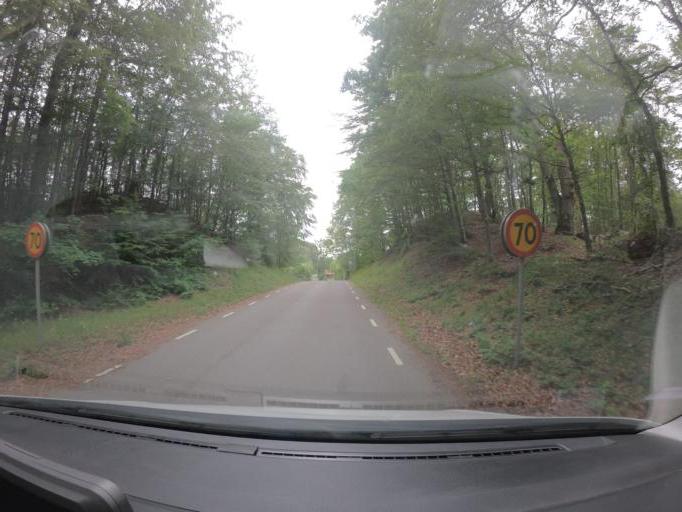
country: SE
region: Skane
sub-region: Perstorps Kommun
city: Perstorp
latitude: 56.1469
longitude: 13.5022
